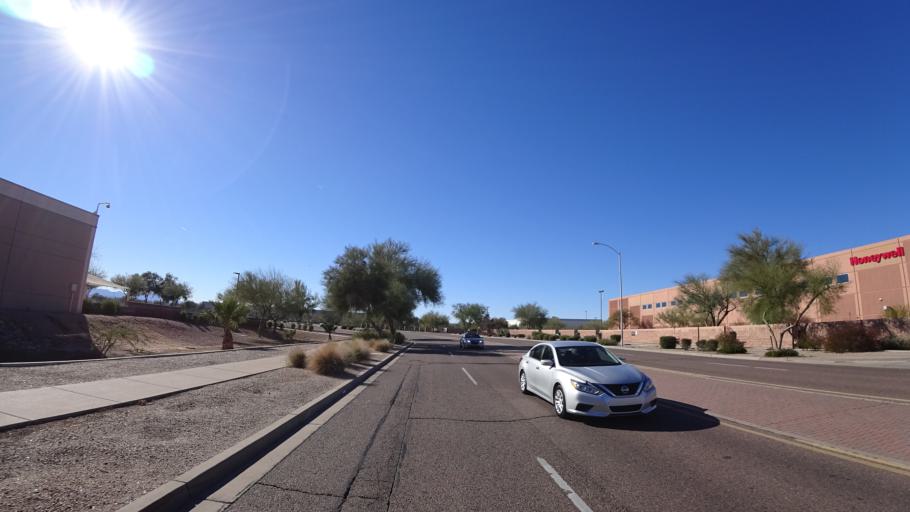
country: US
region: Arizona
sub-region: Maricopa County
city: Phoenix
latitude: 33.4413
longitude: -112.0405
